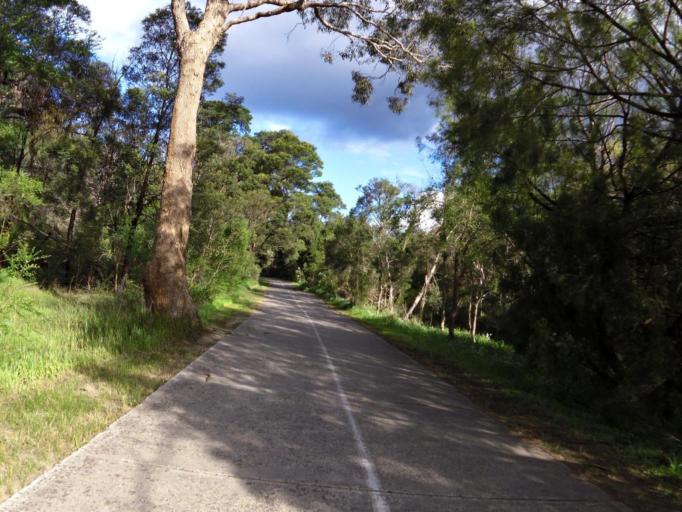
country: AU
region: Victoria
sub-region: Manningham
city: Doncaster East
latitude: -37.7982
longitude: 145.1457
